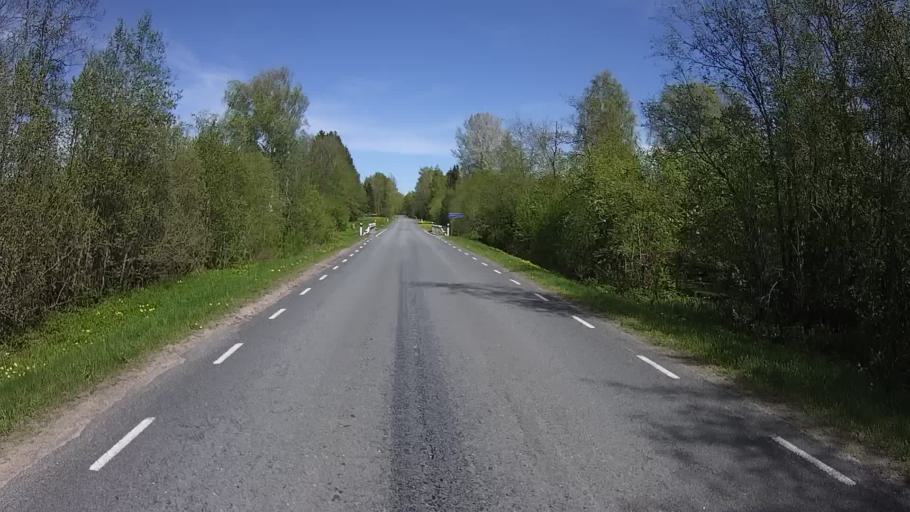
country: LV
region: Apes Novads
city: Ape
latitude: 57.6114
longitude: 26.5752
